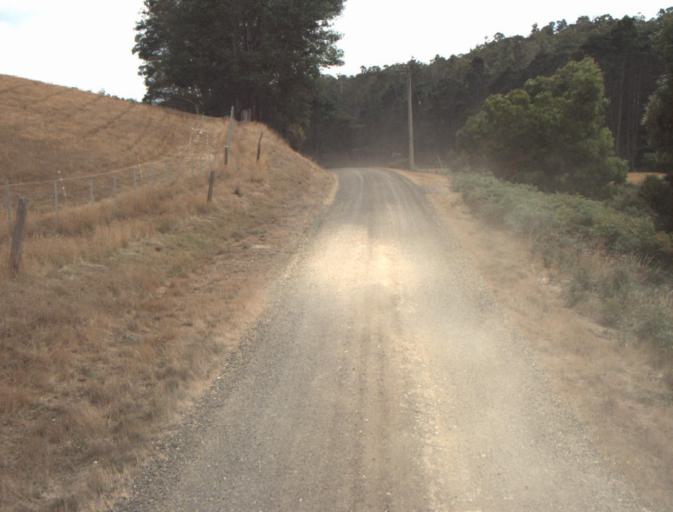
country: AU
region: Tasmania
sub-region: Dorset
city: Bridport
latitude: -41.1865
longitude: 147.2622
